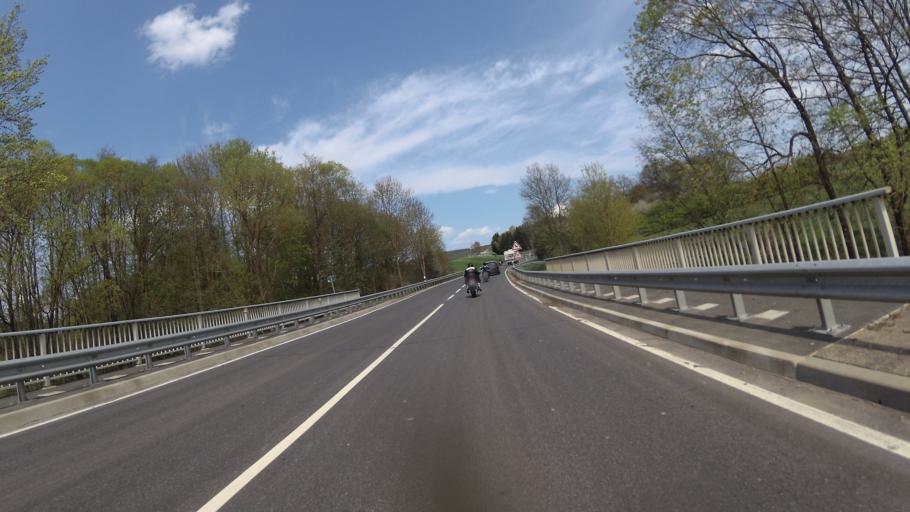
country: DE
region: Rheinland-Pfalz
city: Mullenbach
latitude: 50.3132
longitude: 6.9035
